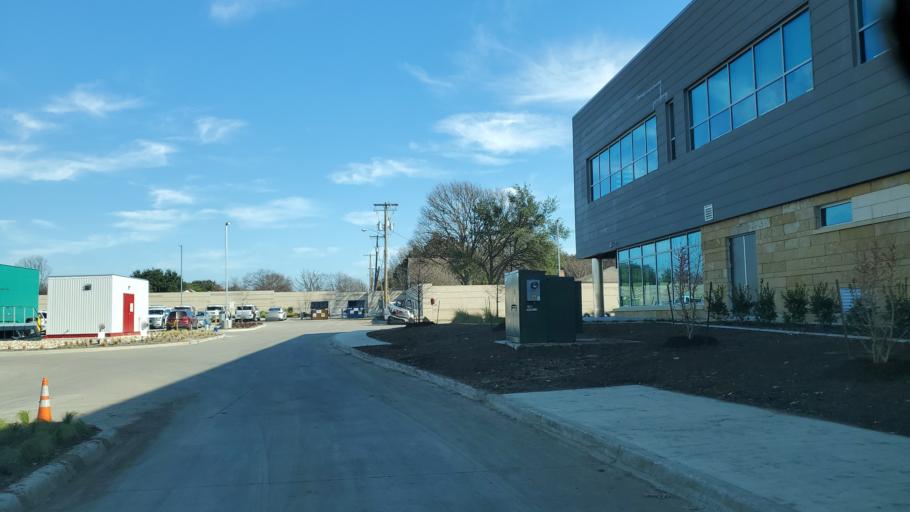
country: US
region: Texas
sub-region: Dallas County
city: Richardson
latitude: 32.9499
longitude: -96.7284
